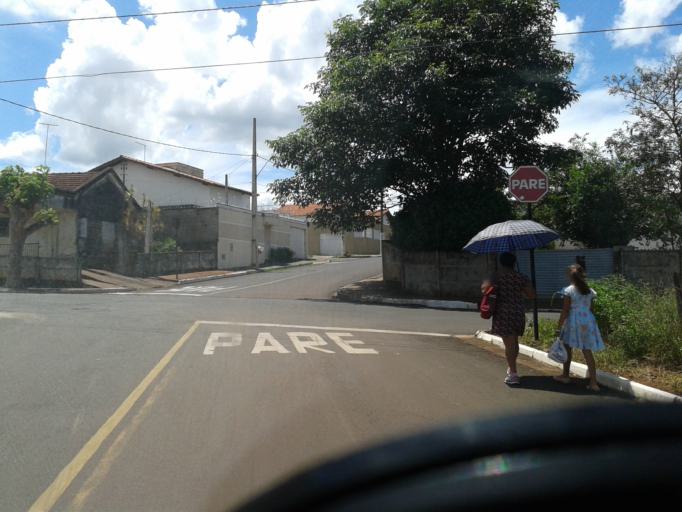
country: BR
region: Minas Gerais
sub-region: Ituiutaba
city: Ituiutaba
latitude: -18.9748
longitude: -49.4691
